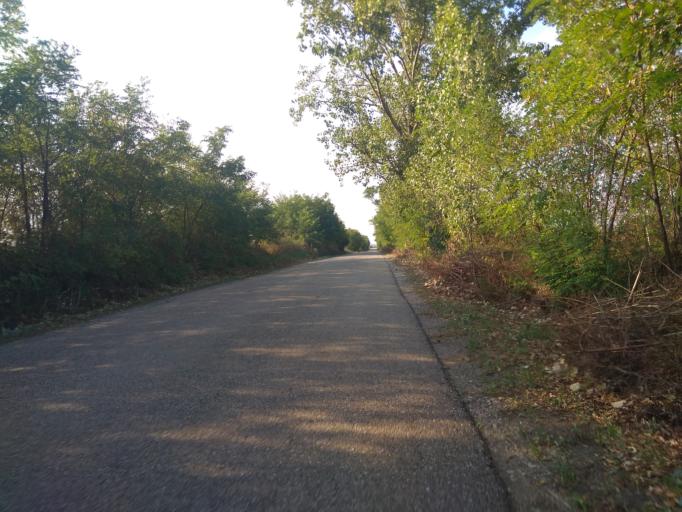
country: HU
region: Borsod-Abauj-Zemplen
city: Harsany
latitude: 47.9106
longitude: 20.7423
